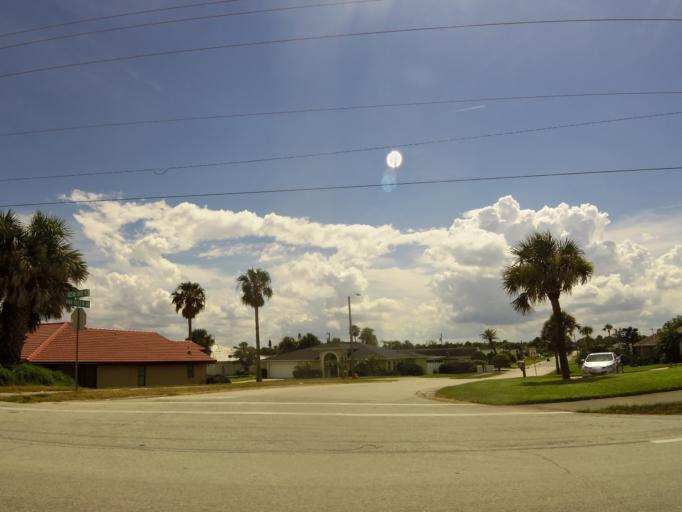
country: US
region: Florida
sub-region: Volusia County
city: Ormond Beach
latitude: 29.3145
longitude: -81.0510
